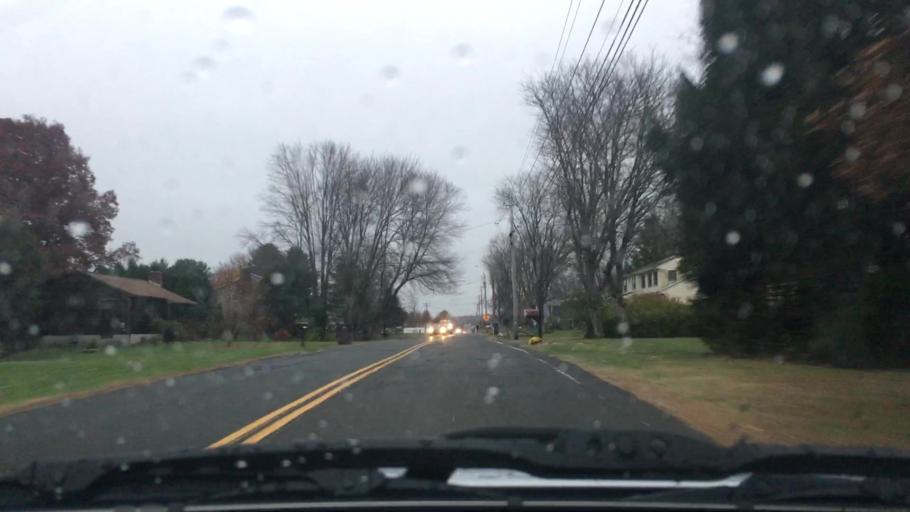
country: US
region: Massachusetts
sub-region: Hampden County
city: Westfield
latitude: 42.1002
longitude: -72.7796
